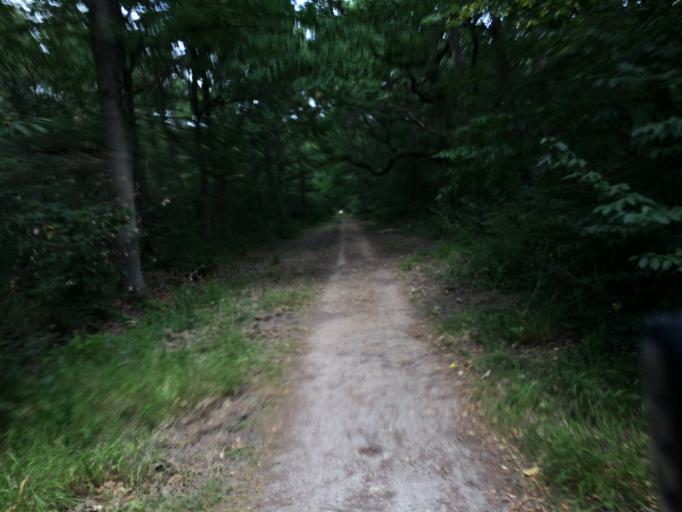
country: FR
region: Ile-de-France
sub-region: Departement de l'Essonne
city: Soisy-sur-Seine
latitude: 48.6693
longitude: 2.4501
